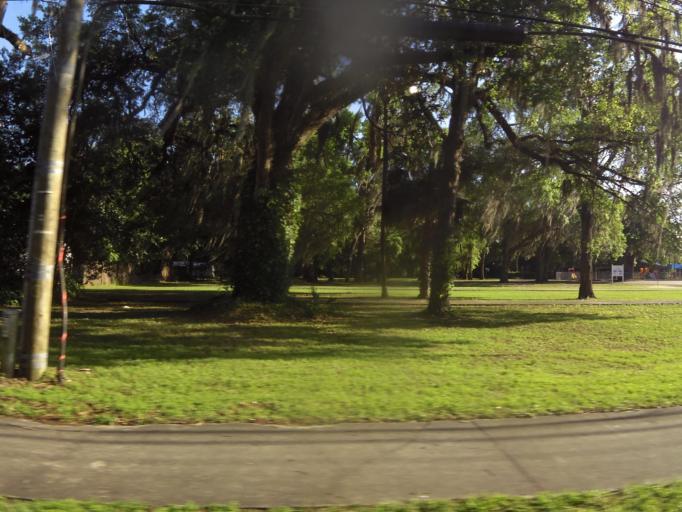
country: US
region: Florida
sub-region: Putnam County
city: Palatka
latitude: 29.6489
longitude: -81.6610
